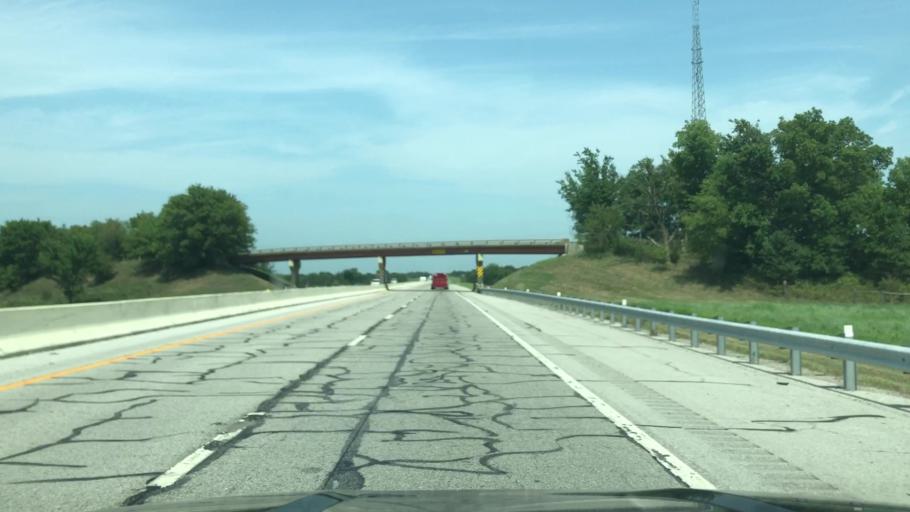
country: US
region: Oklahoma
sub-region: Rogers County
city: Chelsea
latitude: 36.5067
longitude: -95.2750
